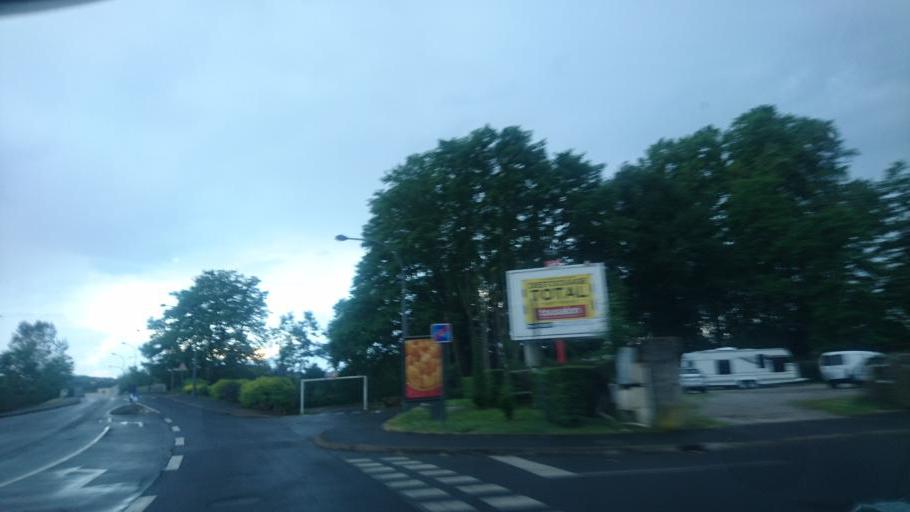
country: FR
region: Limousin
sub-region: Departement de la Correze
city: Malemort-sur-Correze
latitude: 45.1668
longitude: 1.5609
